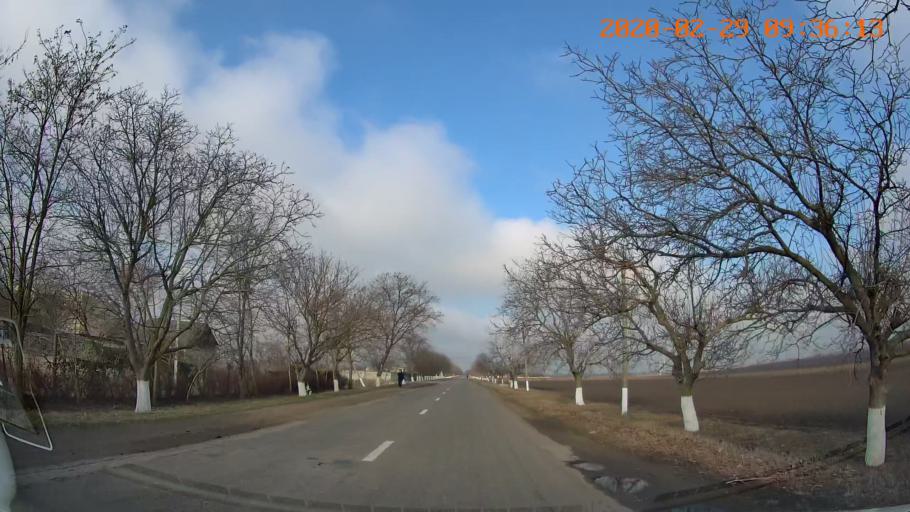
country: MD
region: Telenesti
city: Dnestrovsc
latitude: 46.6231
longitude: 29.8909
